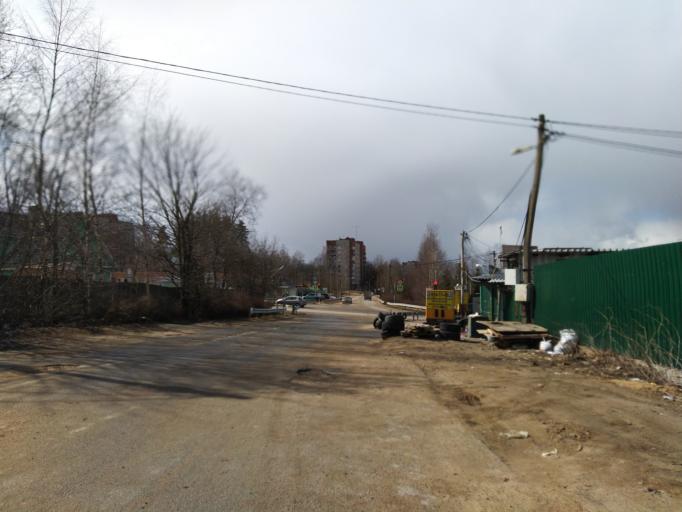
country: RU
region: Leningrad
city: Toksovo
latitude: 60.1118
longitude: 30.5023
